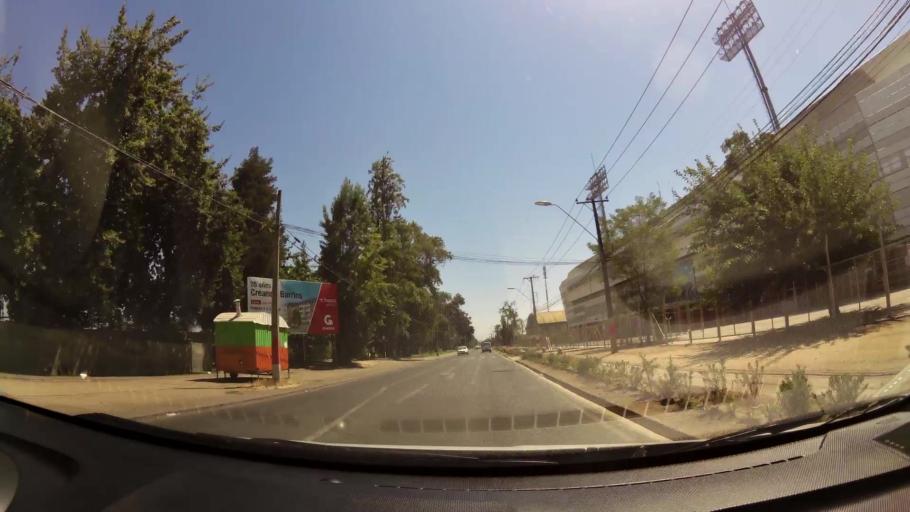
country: CL
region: Maule
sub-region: Provincia de Curico
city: Curico
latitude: -34.9748
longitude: -71.2318
